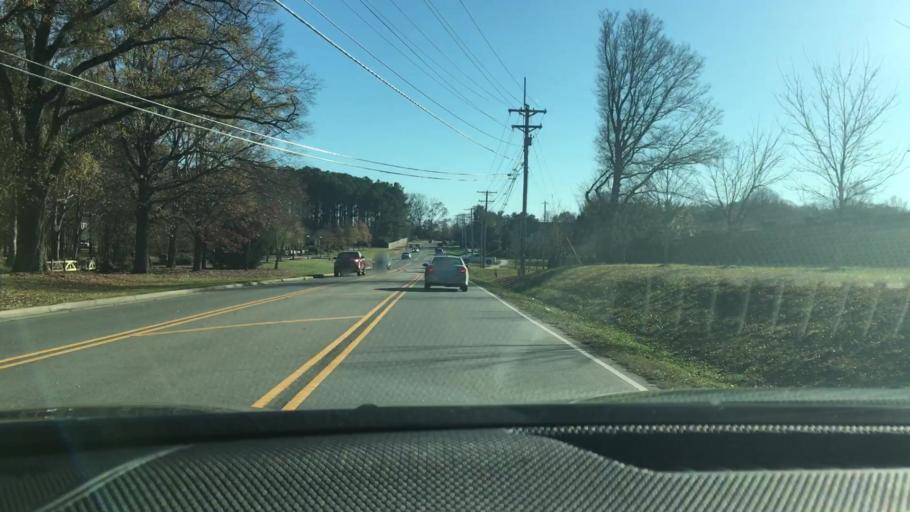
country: US
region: North Carolina
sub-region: Mecklenburg County
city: Cornelius
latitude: 35.4556
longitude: -80.8886
